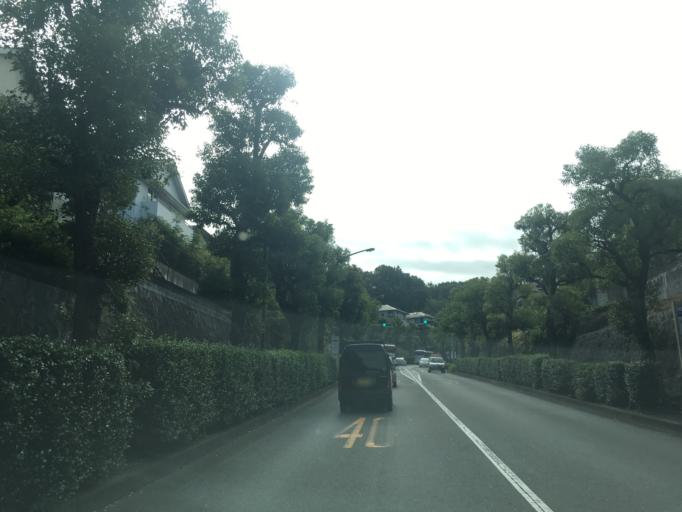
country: JP
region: Tokyo
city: Hino
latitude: 35.6442
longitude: 139.3867
